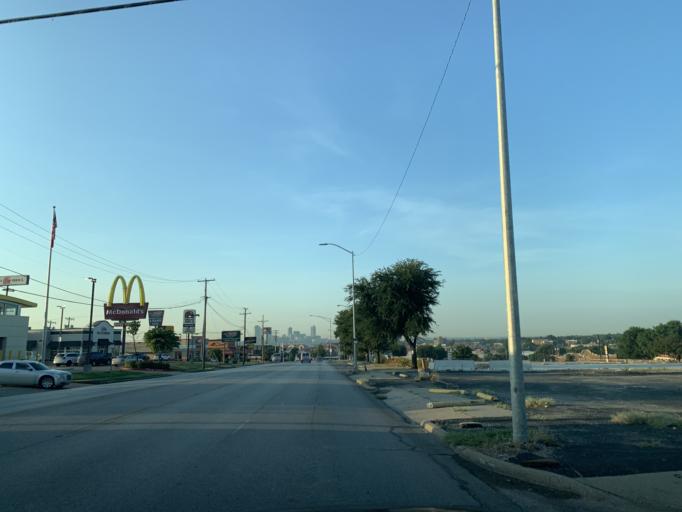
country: US
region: Texas
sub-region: Tarrant County
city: River Oaks
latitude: 32.7976
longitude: -97.3499
